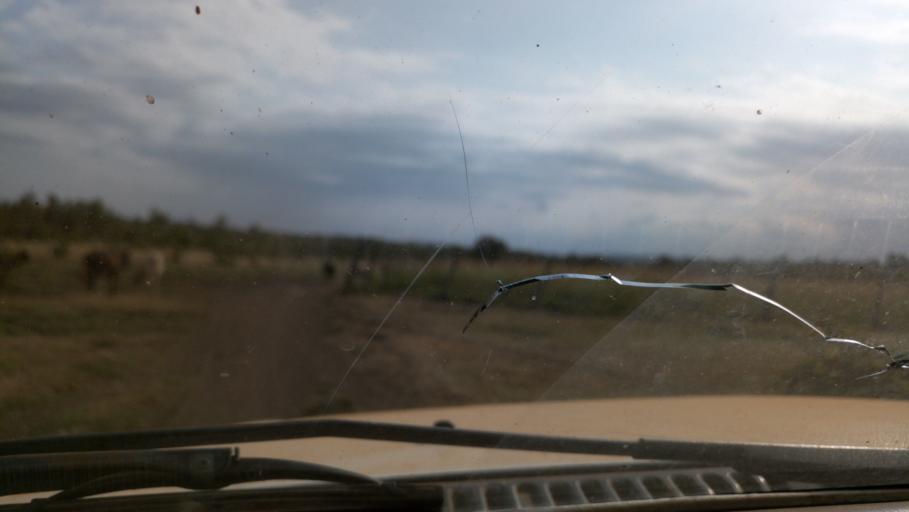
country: KE
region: Murang'a District
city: Karuri
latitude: -0.7473
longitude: 37.2216
